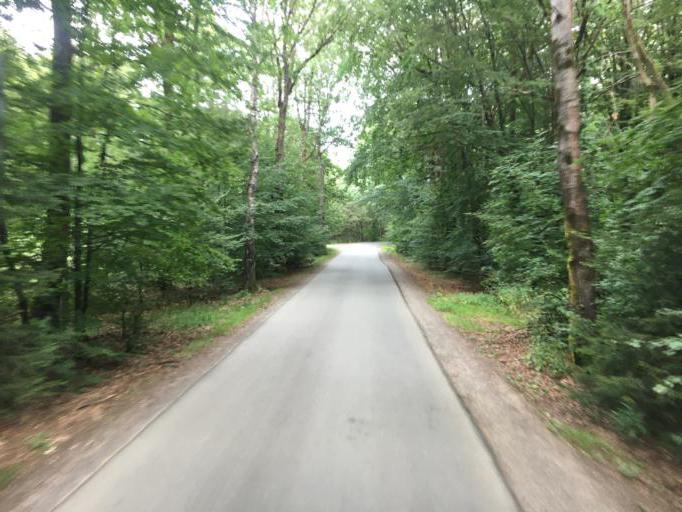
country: DE
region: North Rhine-Westphalia
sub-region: Regierungsbezirk Arnsberg
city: Herscheid
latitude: 51.2099
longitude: 7.7693
